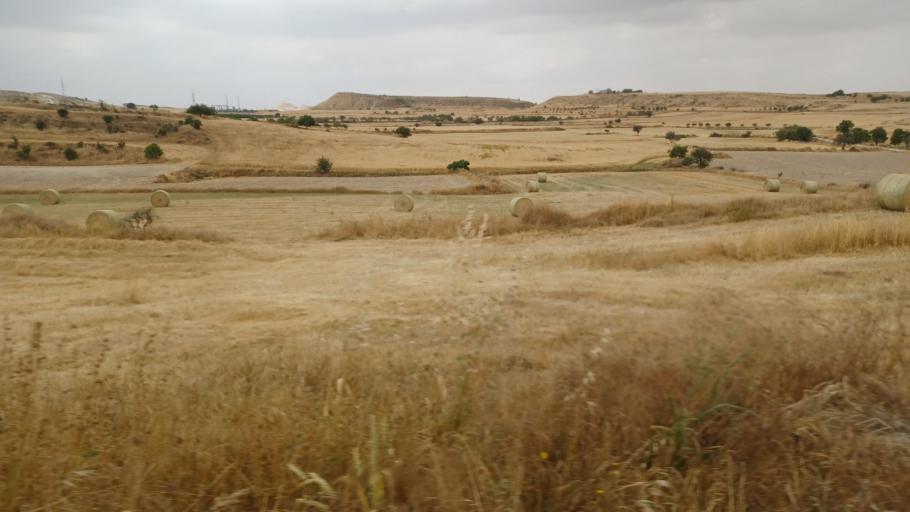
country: CY
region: Larnaka
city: Athienou
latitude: 35.0401
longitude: 33.5725
